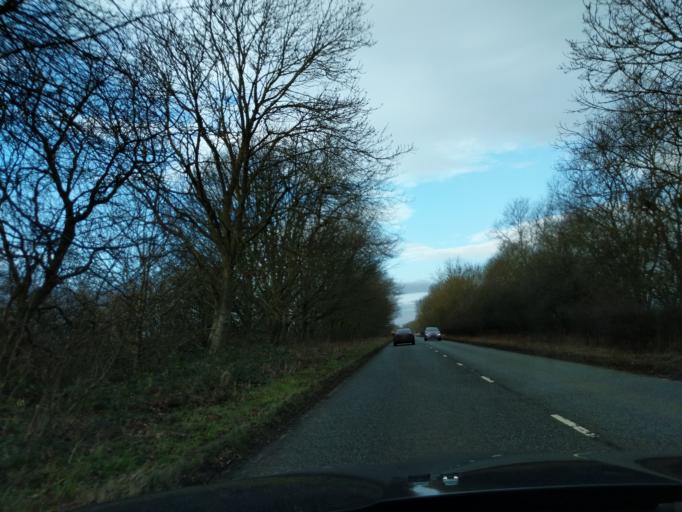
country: GB
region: England
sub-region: Northumberland
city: Darras Hall
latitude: 55.0730
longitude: -1.7951
